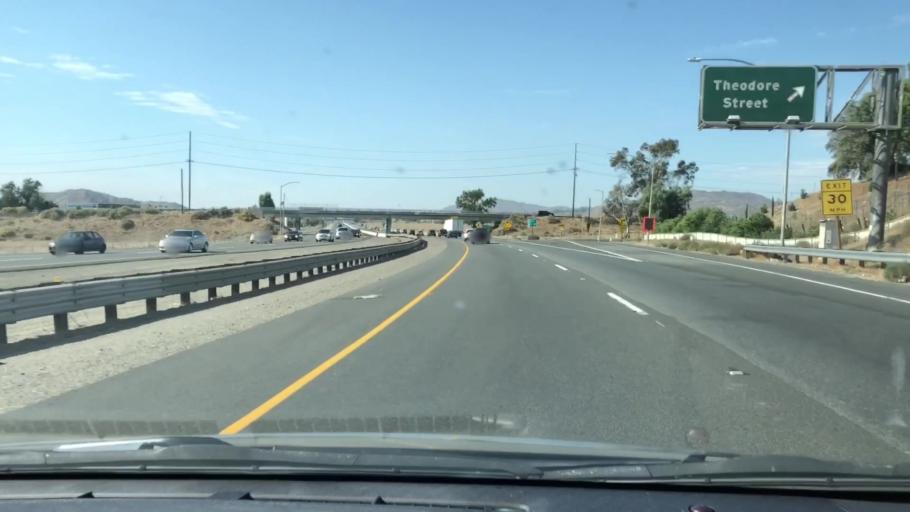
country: US
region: California
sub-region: Riverside County
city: Moreno Valley
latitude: 33.9392
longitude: -117.1367
